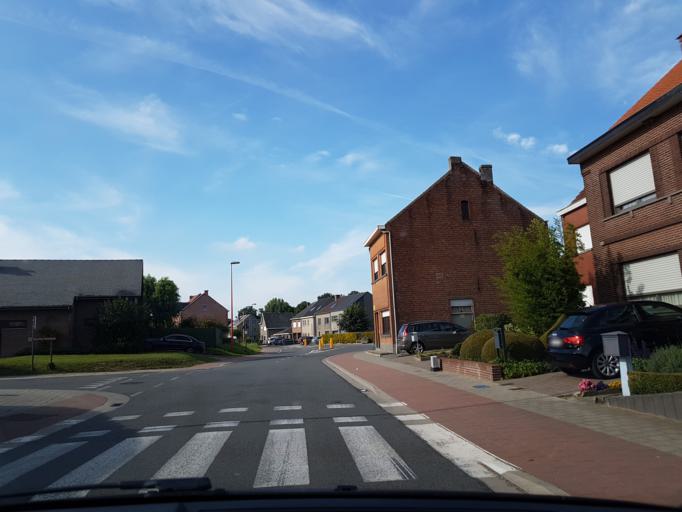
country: BE
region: Flanders
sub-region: Provincie Vlaams-Brabant
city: Grimbergen
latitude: 50.9728
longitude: 4.3904
